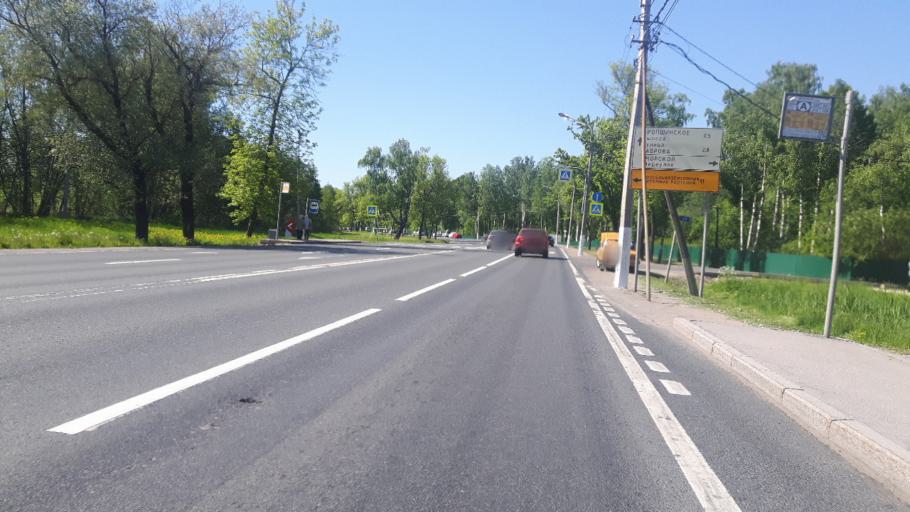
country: RU
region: Leningrad
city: Gorbunki
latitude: 59.8706
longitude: 29.9704
